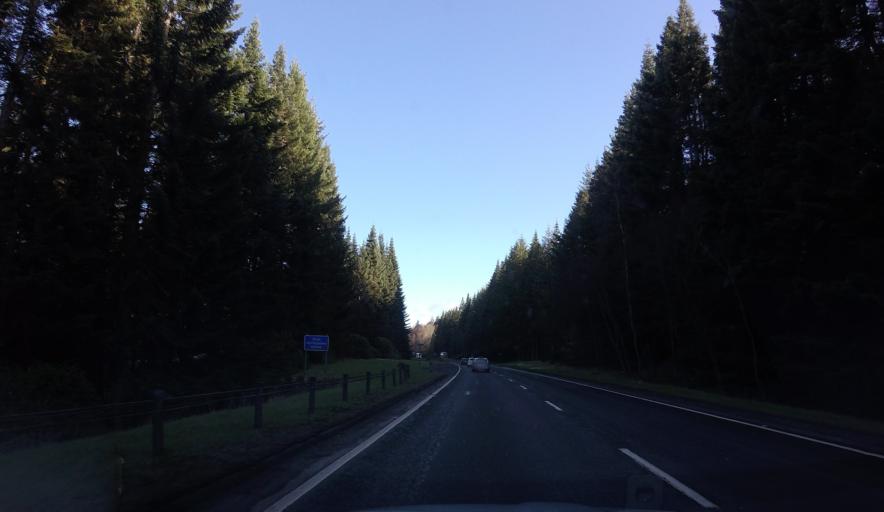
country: GB
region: Scotland
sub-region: Perth and Kinross
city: Bankfoot
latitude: 56.5416
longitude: -3.5497
